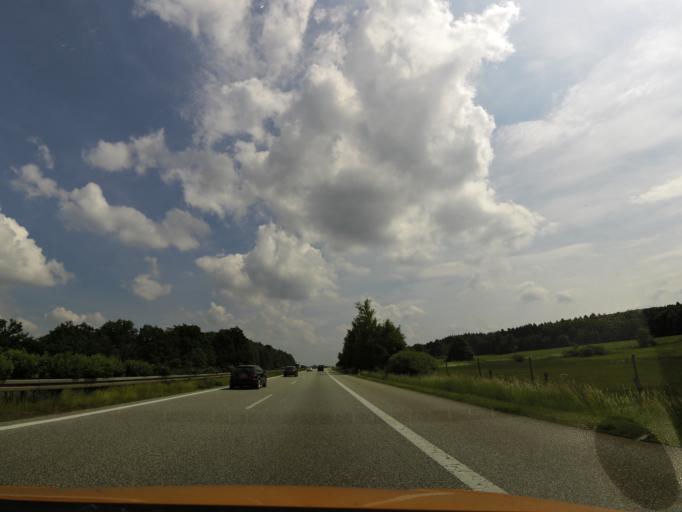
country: DE
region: Mecklenburg-Vorpommern
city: Siggelkow
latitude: 53.3241
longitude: 11.8871
